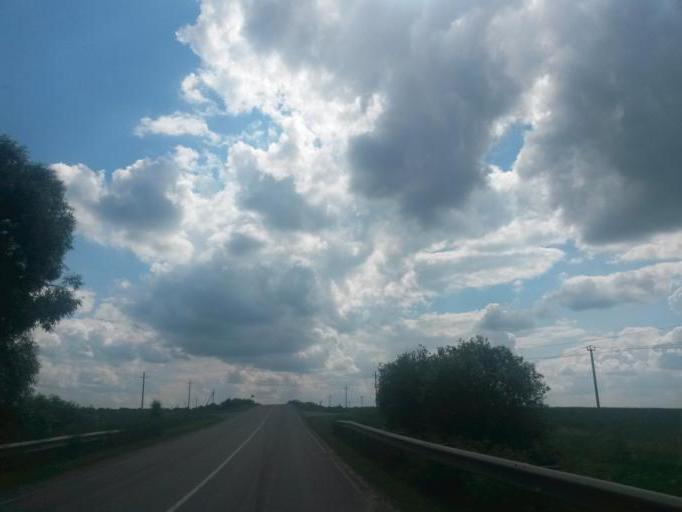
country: RU
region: Moskovskaya
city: Barybino
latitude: 55.2216
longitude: 37.7895
